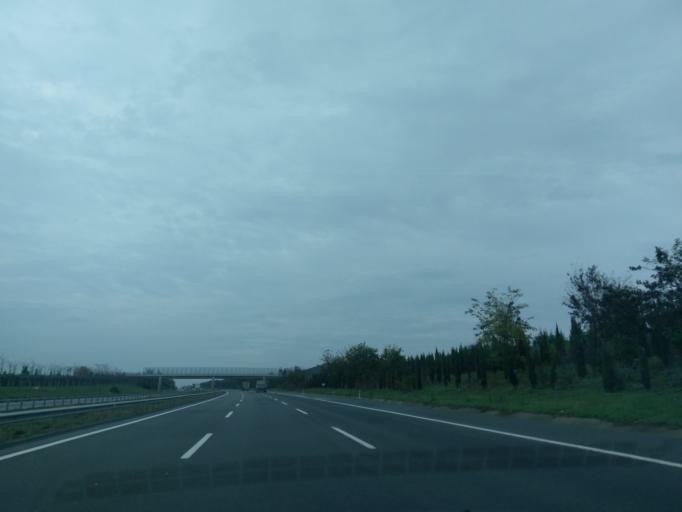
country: TR
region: Istanbul
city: Canta
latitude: 41.1590
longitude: 28.1383
